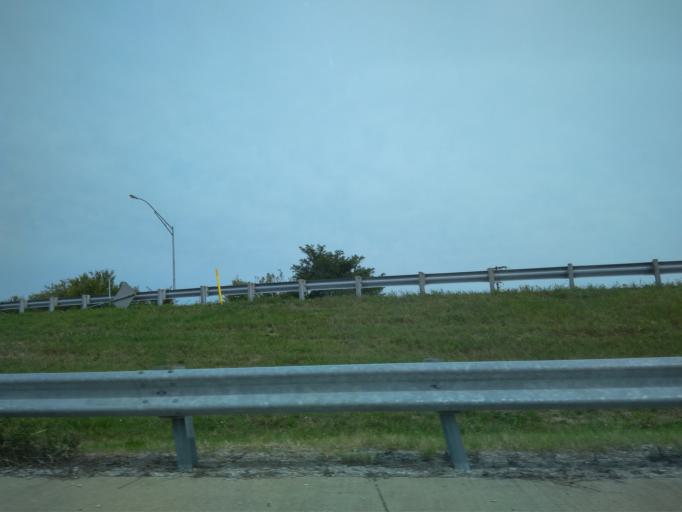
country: US
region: Kentucky
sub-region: Jefferson County
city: Audubon Park
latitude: 38.1917
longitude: -85.7373
